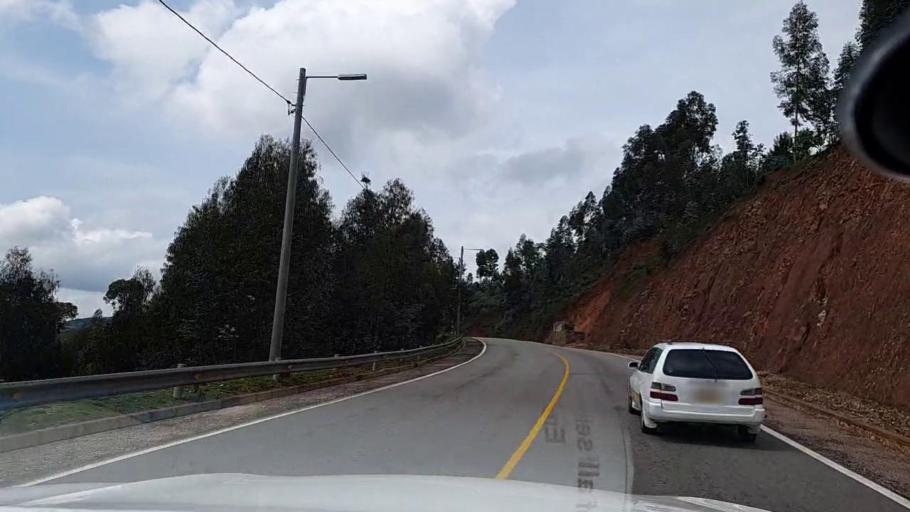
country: RW
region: Southern Province
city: Nzega
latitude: -2.5128
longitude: 29.4640
